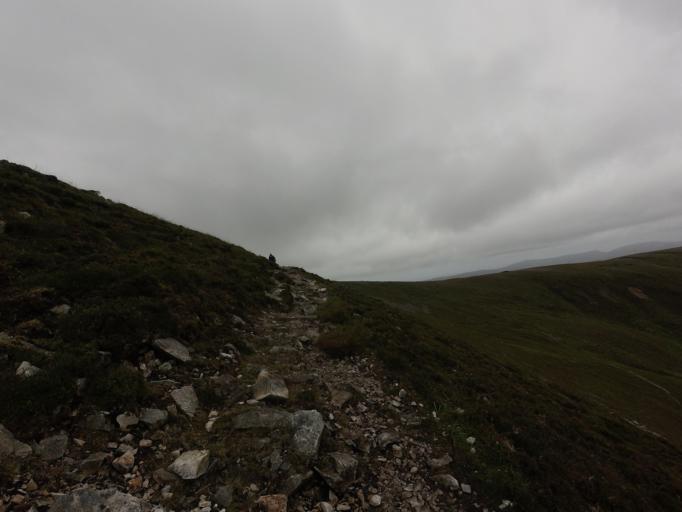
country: IE
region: Ulster
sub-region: County Donegal
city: Killybegs
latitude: 54.6458
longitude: -8.6885
